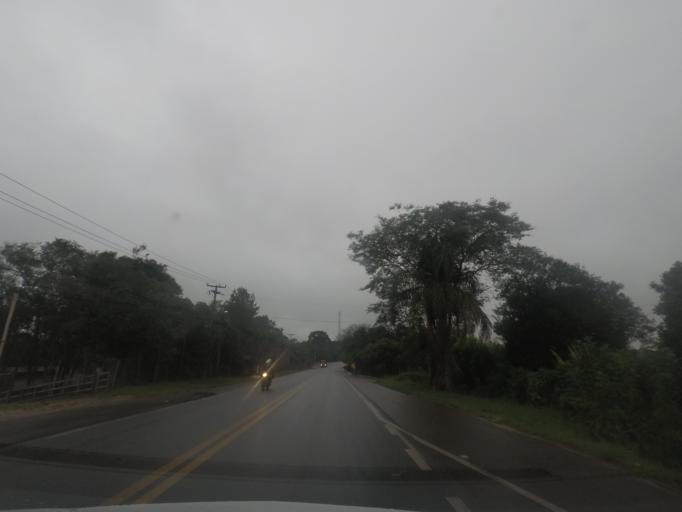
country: BR
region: Parana
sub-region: Colombo
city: Colombo
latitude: -25.3142
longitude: -49.1513
